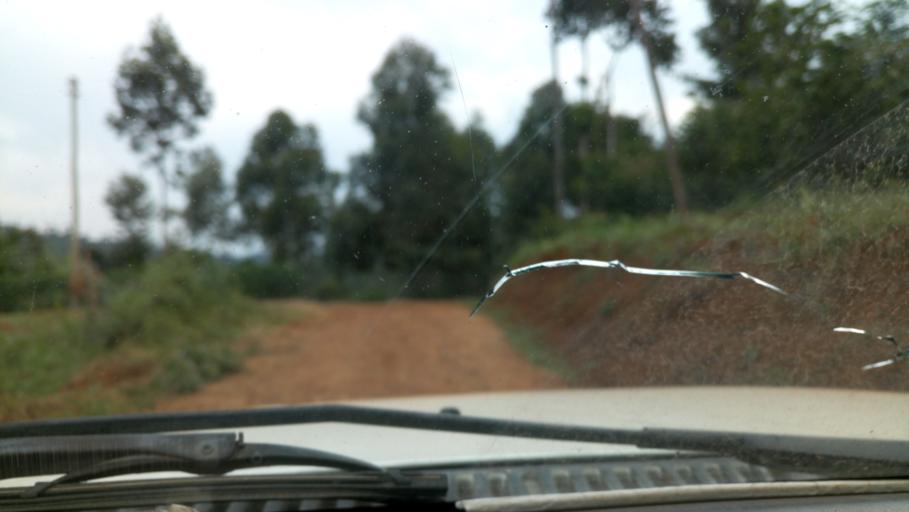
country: KE
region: Murang'a District
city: Kangema
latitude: -0.6470
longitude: 36.9459
